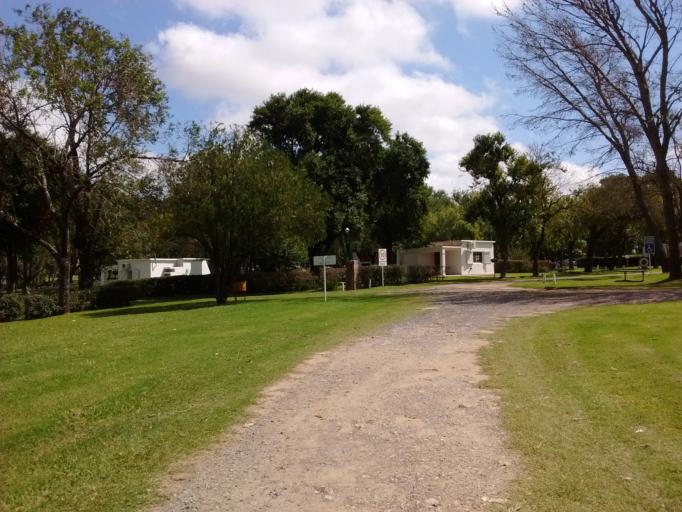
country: AR
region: Santa Fe
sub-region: Departamento de San Lorenzo
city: San Lorenzo
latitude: -32.6381
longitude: -60.8182
